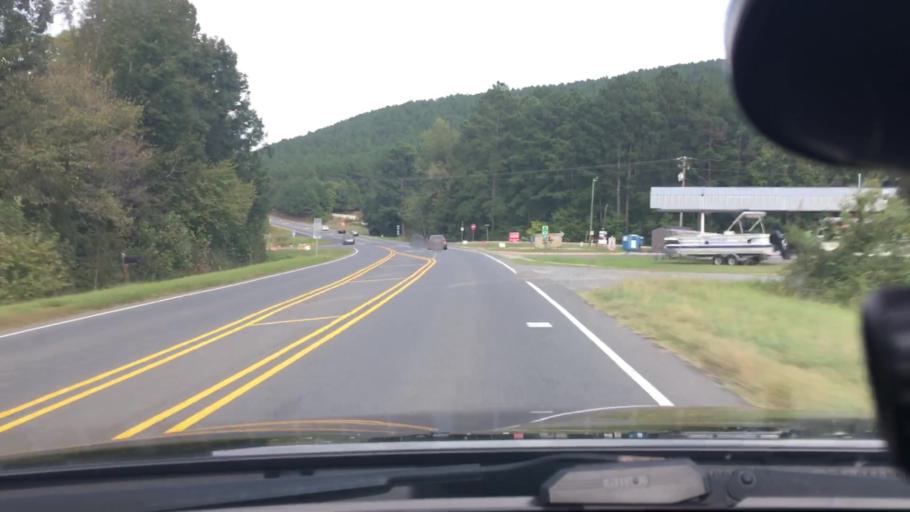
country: US
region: North Carolina
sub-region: Stanly County
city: Norwood
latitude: 35.3073
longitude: -80.0606
